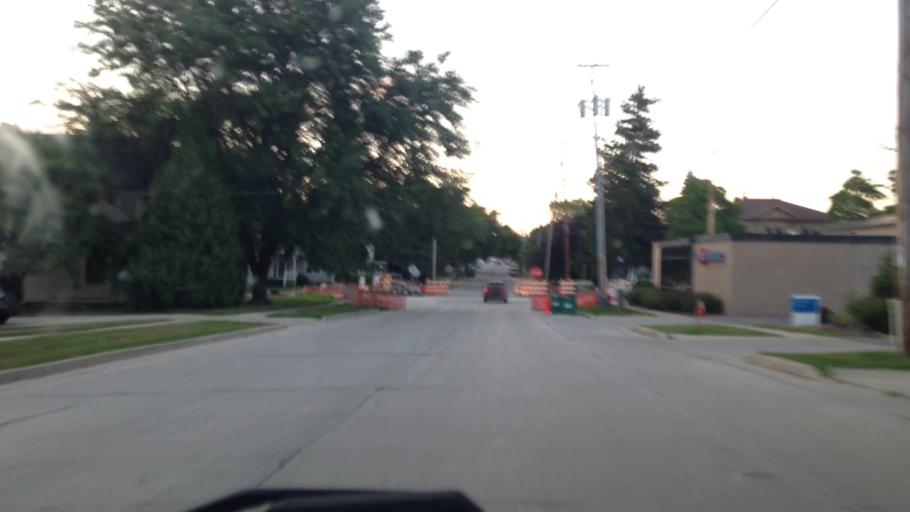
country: US
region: Wisconsin
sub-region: Dodge County
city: Mayville
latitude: 43.4932
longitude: -88.5470
